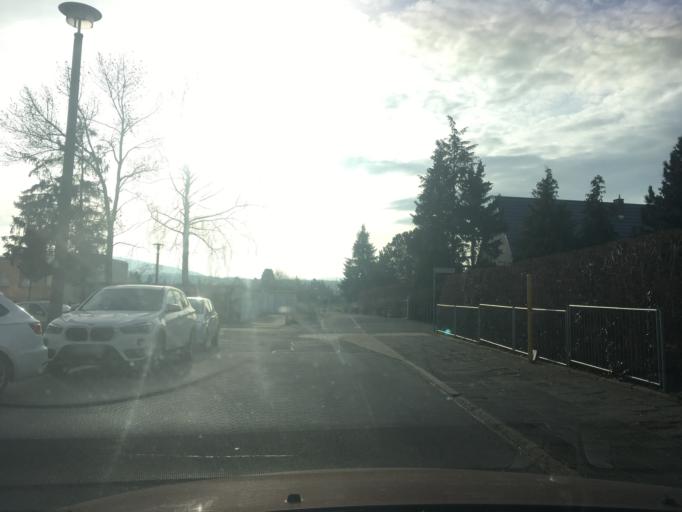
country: DE
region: Saxony
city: Bautzen
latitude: 51.1729
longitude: 14.4514
